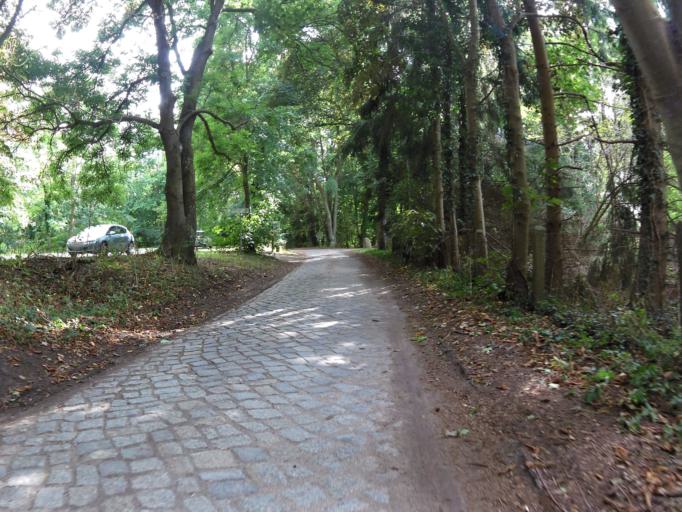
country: DE
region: Mecklenburg-Vorpommern
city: Loddin
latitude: 54.0005
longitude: 14.0598
